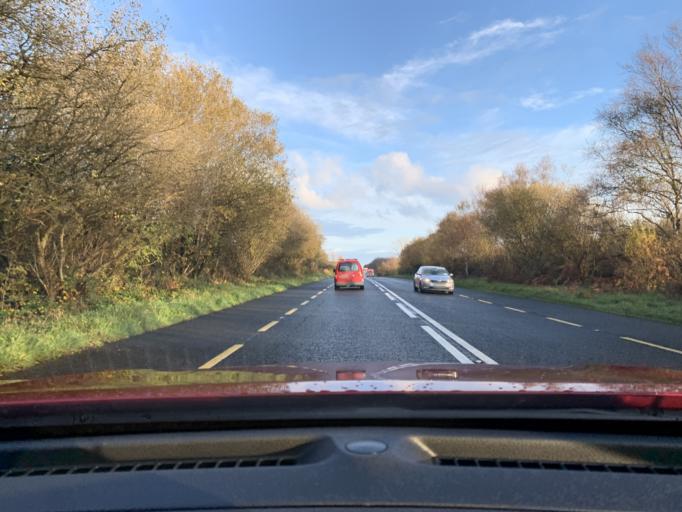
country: IE
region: Connaught
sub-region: Sligo
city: Sligo
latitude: 54.3765
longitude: -8.5289
